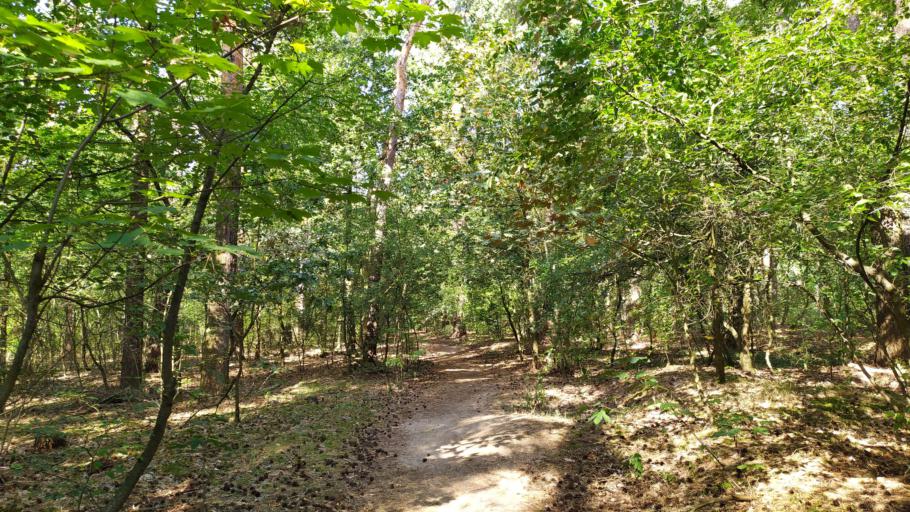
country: DE
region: Berlin
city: Berlin Koepenick
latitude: 52.4358
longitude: 13.5986
